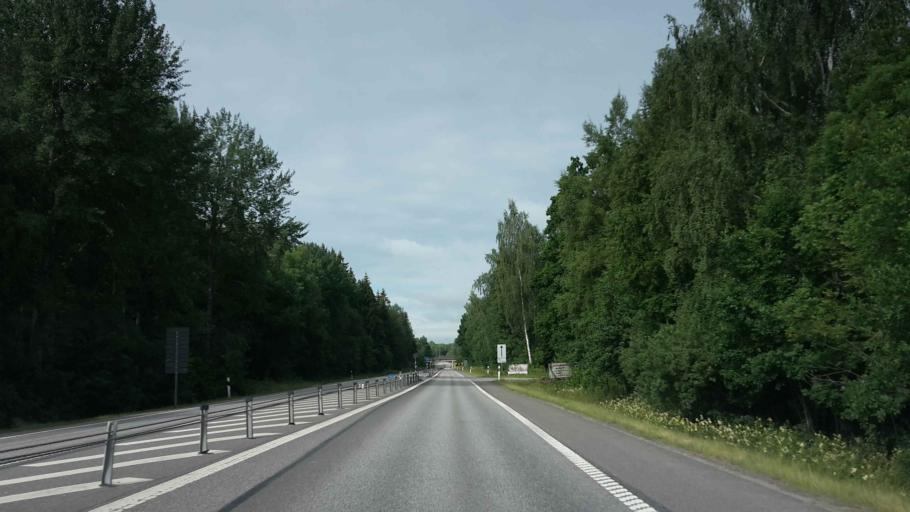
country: SE
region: OEstergoetland
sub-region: Motala Kommun
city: Motala
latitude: 58.5735
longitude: 15.0821
